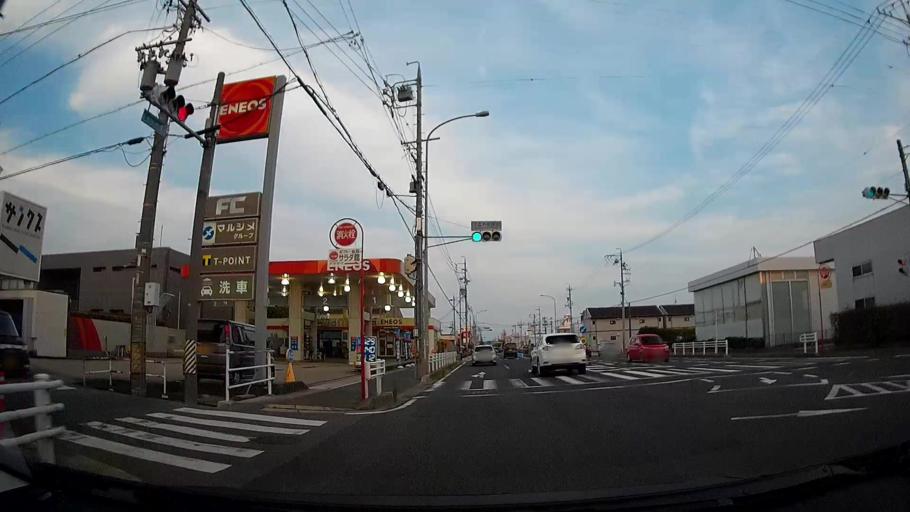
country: JP
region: Aichi
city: Kozakai-cho
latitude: 34.7894
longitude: 137.3744
